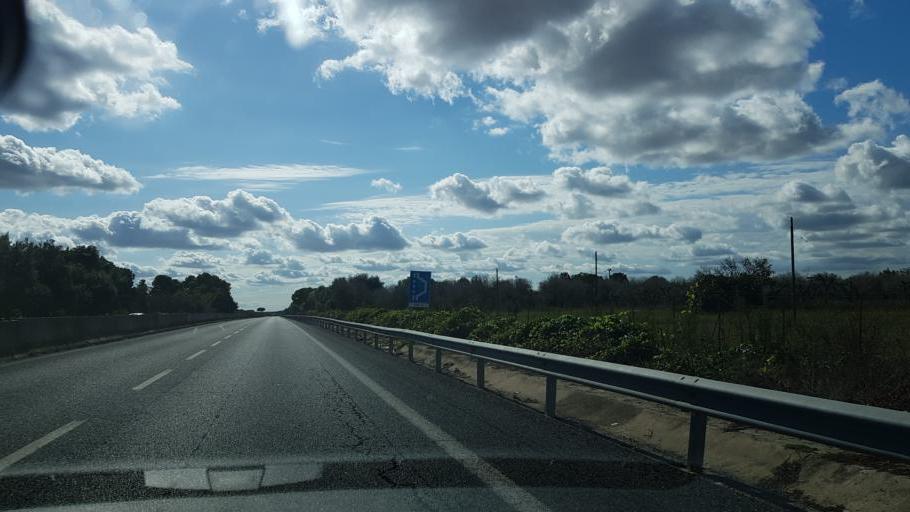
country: IT
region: Apulia
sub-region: Provincia di Brindisi
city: Torchiarolo
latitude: 40.4802
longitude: 18.0447
